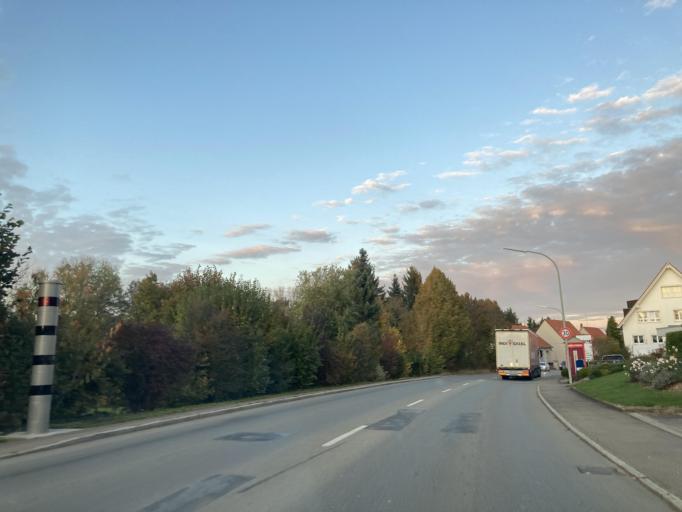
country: DE
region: Baden-Wuerttemberg
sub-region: Tuebingen Region
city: Balingen
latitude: 48.2543
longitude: 8.8347
